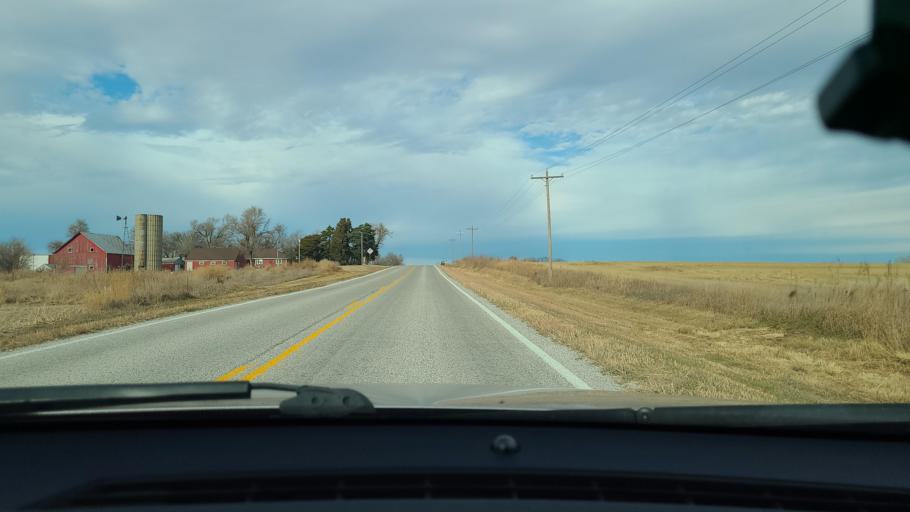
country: US
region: Kansas
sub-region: McPherson County
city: Inman
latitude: 38.2933
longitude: -97.9250
